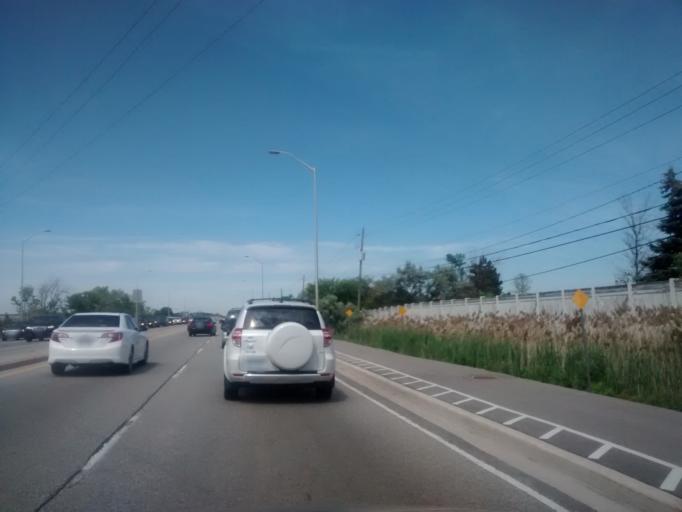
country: CA
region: Ontario
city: Burlington
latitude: 43.4010
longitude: -79.8139
